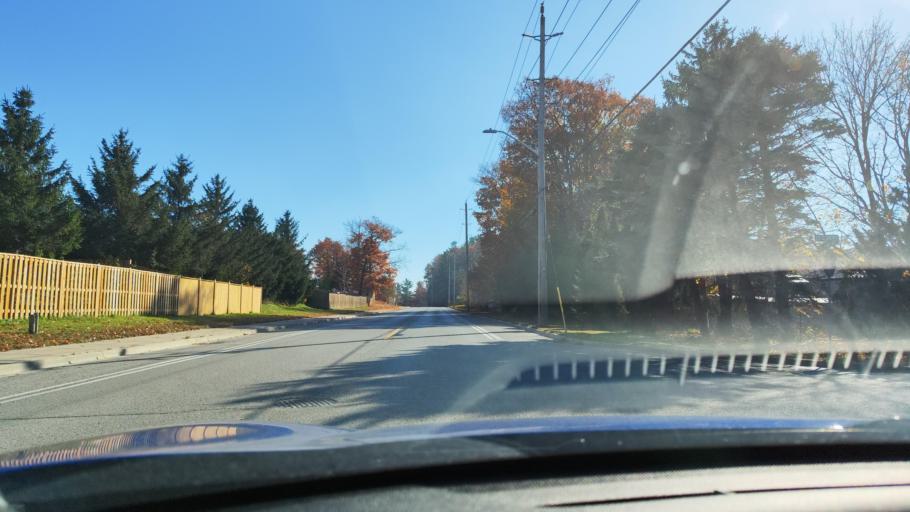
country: CA
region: Ontario
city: Wasaga Beach
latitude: 44.5220
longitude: -79.9983
